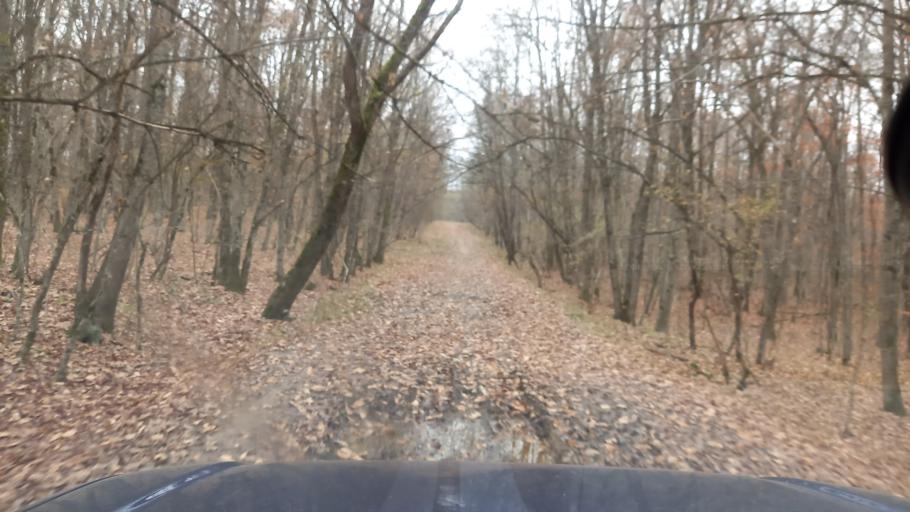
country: RU
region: Krasnodarskiy
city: Goryachiy Klyuch
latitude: 44.5089
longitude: 39.2917
